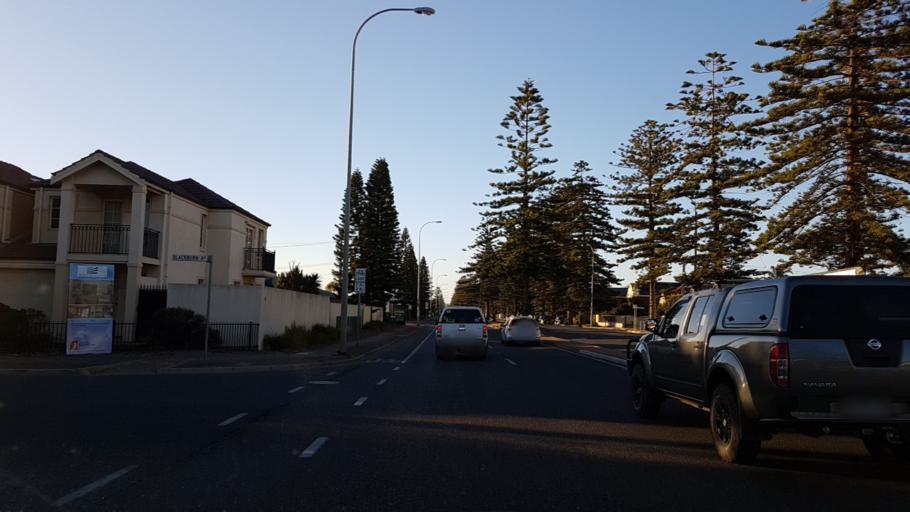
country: AU
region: South Australia
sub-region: Adelaide
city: Glenelg
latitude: -34.9650
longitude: 138.5168
